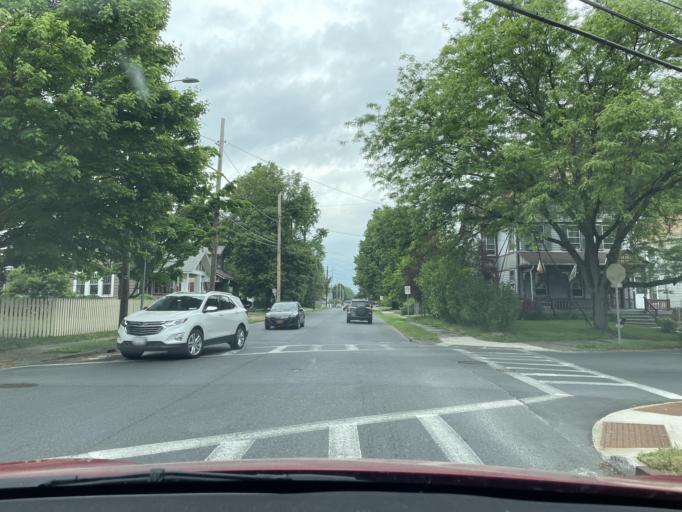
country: US
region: New York
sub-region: Ulster County
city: Kingston
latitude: 41.9300
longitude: -74.0209
